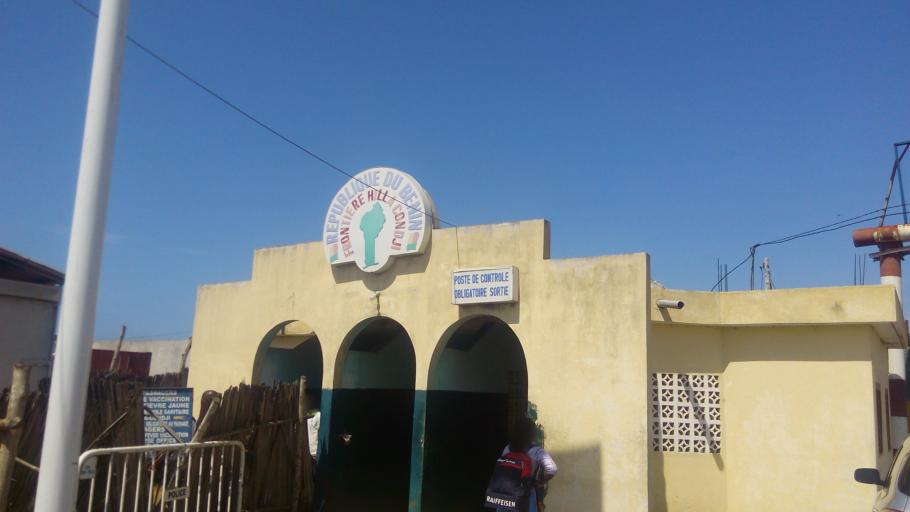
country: TG
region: Maritime
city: Aneho
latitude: 6.2406
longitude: 1.6301
